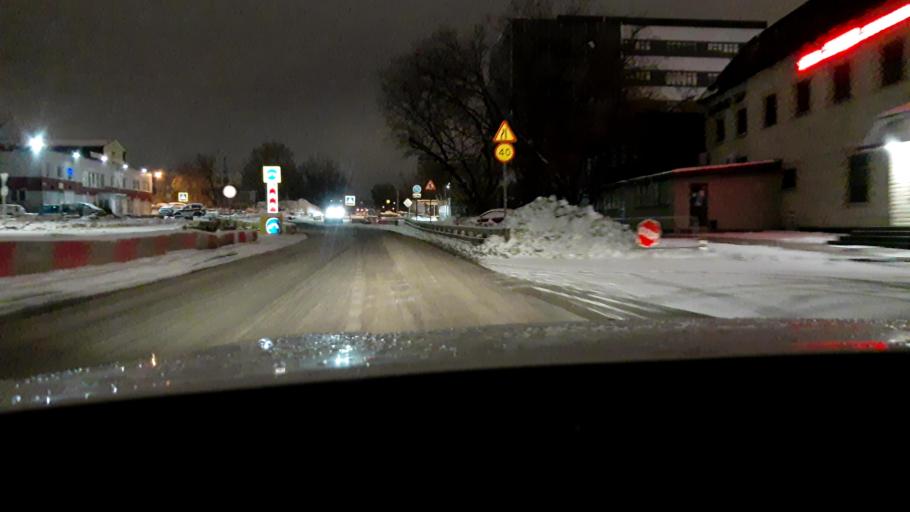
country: RU
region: Moscow
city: Khimki
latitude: 55.9033
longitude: 37.4254
